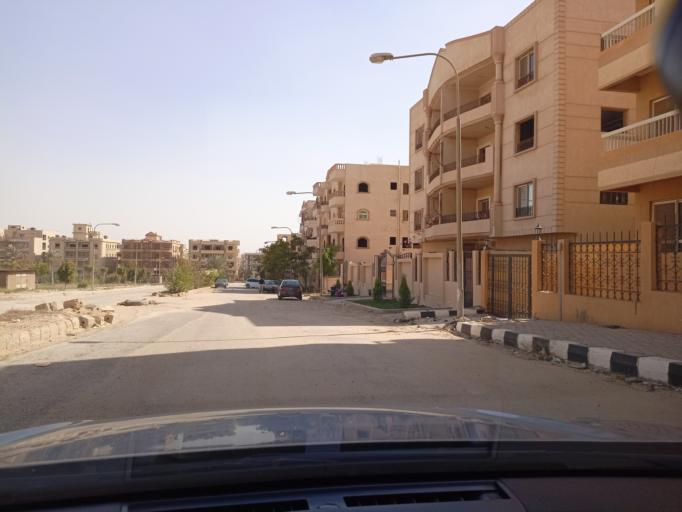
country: EG
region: Muhafazat al Qalyubiyah
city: Al Khankah
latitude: 30.2179
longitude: 31.4418
